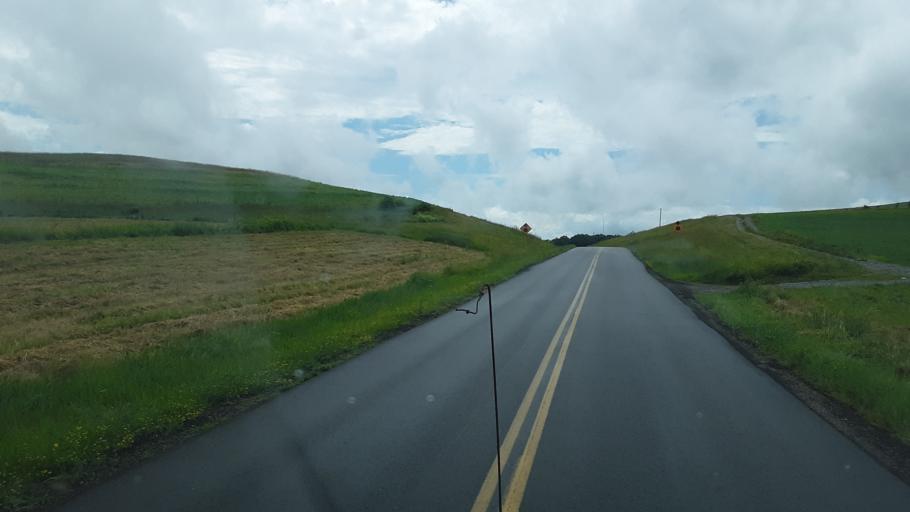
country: US
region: Ohio
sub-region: Carroll County
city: Carrollton
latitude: 40.6203
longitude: -81.0642
